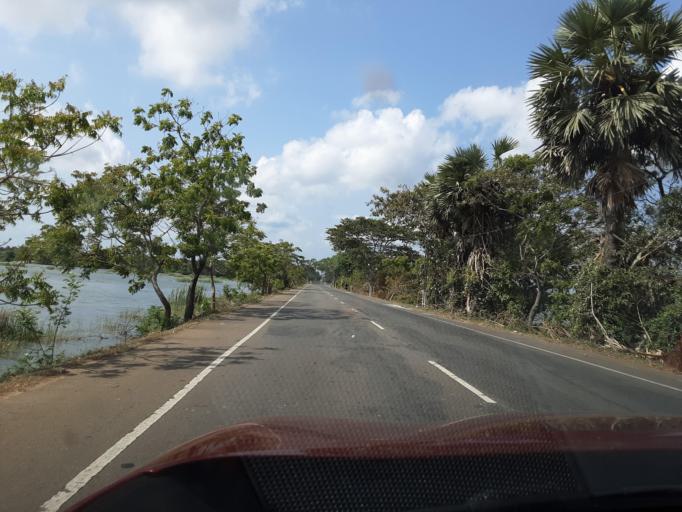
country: LK
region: Southern
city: Tangalla
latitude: 6.2901
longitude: 81.2346
